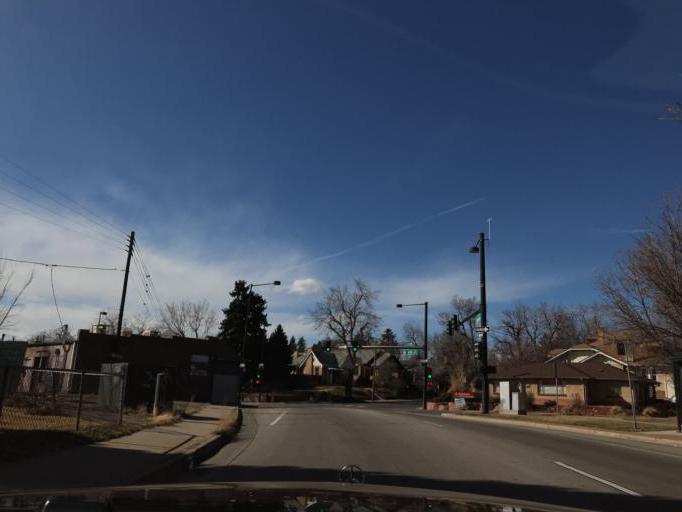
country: US
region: Colorado
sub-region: Denver County
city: Denver
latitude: 39.7251
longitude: -104.9584
